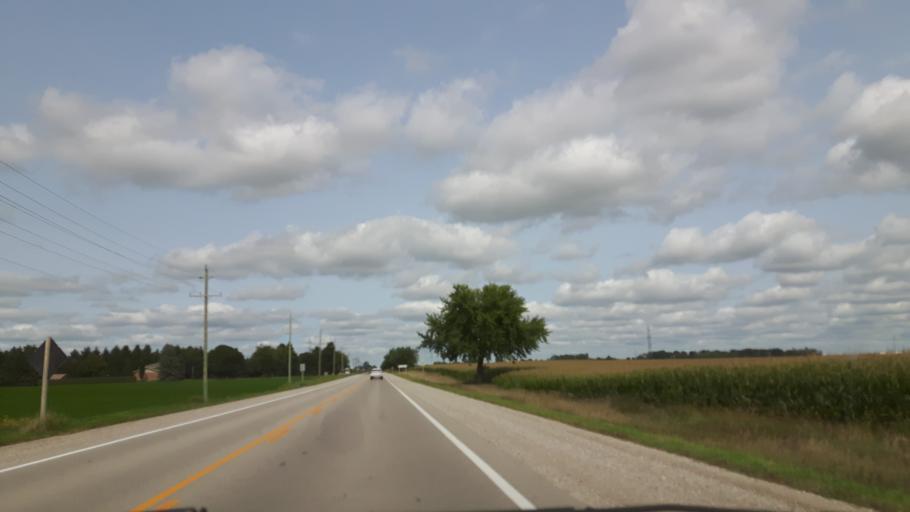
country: CA
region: Ontario
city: Huron East
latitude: 43.5646
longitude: -81.3839
